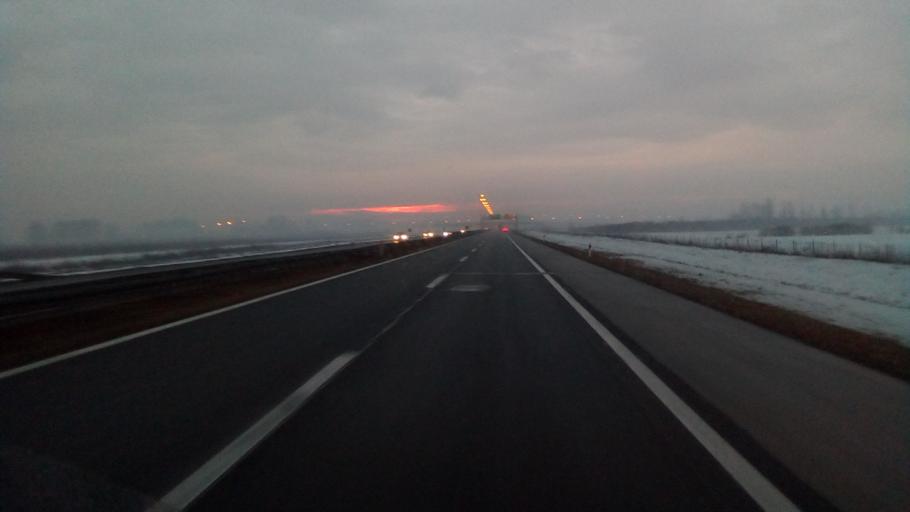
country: HR
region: Zagrebacka
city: Brckovljani
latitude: 45.7686
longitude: 16.2172
